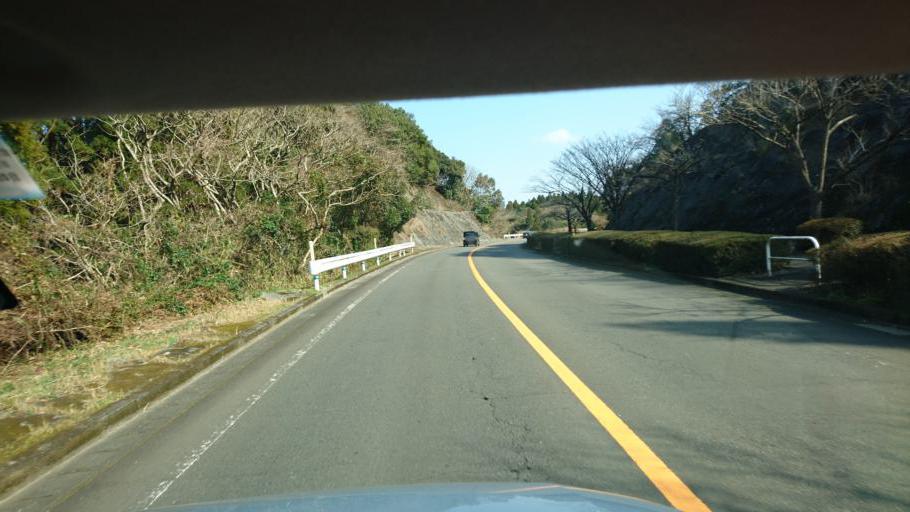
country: JP
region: Miyazaki
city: Miyazaki-shi
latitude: 31.8352
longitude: 131.4051
